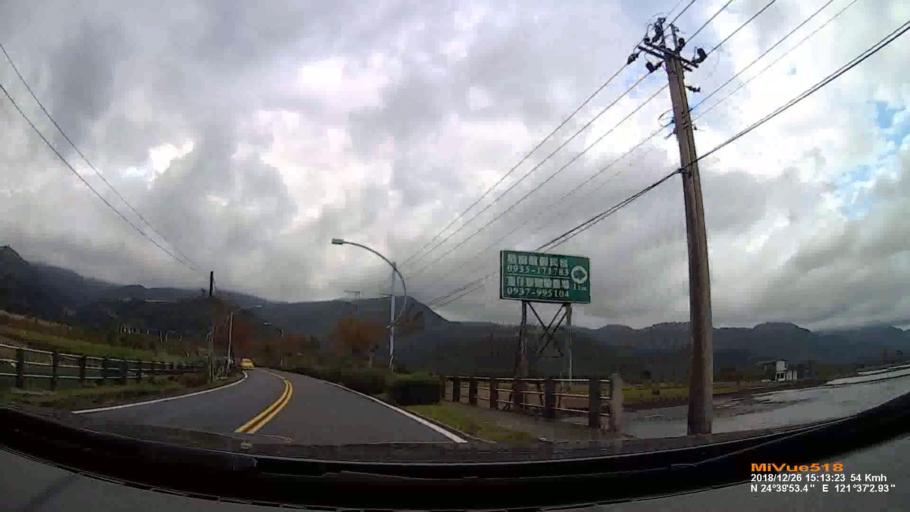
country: TW
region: Taiwan
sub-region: Yilan
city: Yilan
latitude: 24.6672
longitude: 121.5925
